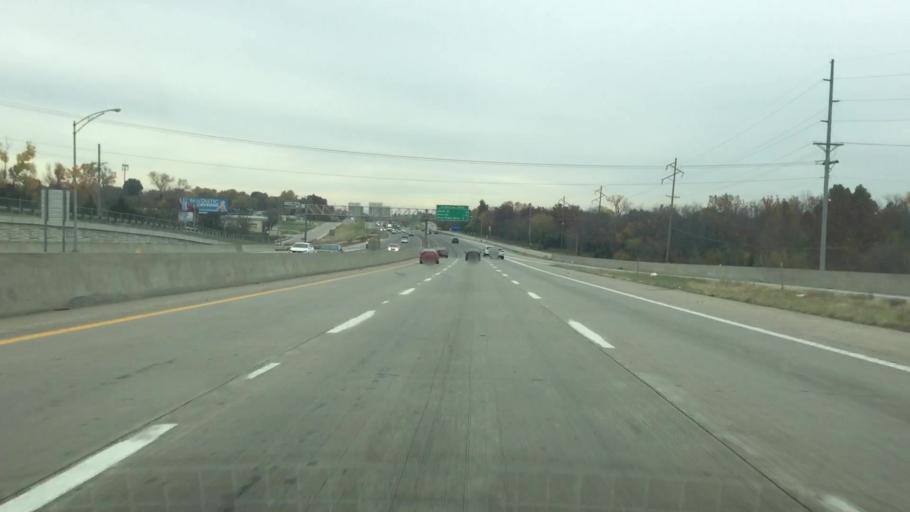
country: US
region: Missouri
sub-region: Jackson County
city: Grandview
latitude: 38.8602
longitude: -94.5275
